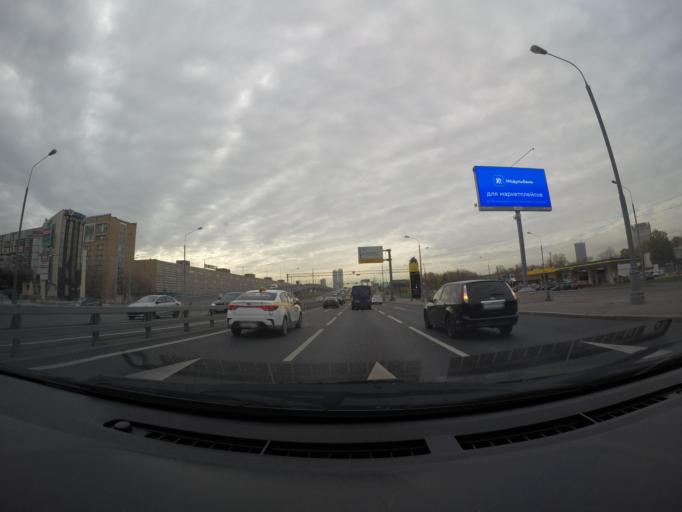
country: RU
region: Moscow
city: Rostokino
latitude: 55.8518
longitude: 37.6782
